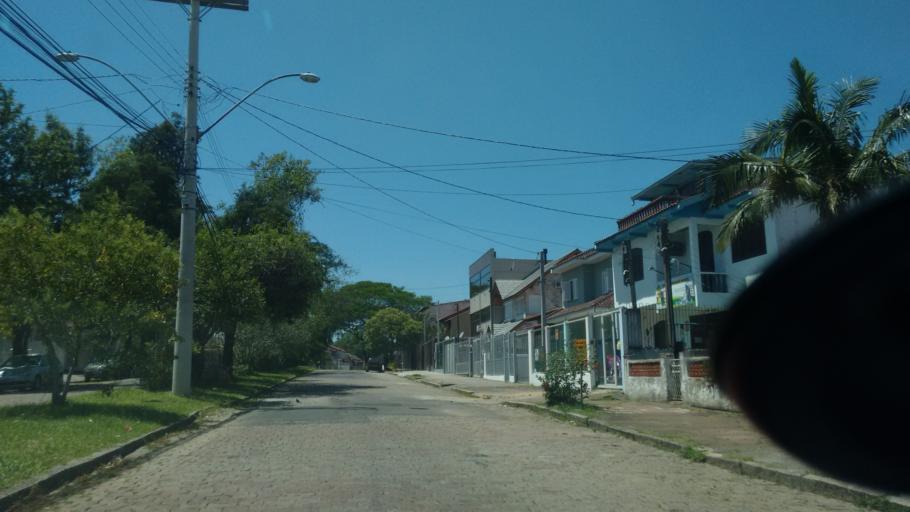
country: BR
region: Rio Grande do Sul
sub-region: Cachoeirinha
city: Cachoeirinha
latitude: -29.9971
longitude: -51.1268
